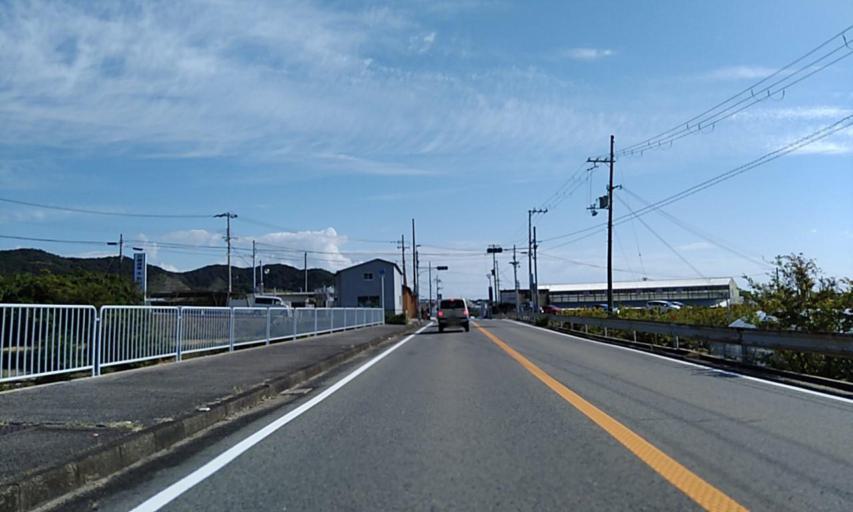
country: JP
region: Wakayama
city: Gobo
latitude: 33.8330
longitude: 135.1807
